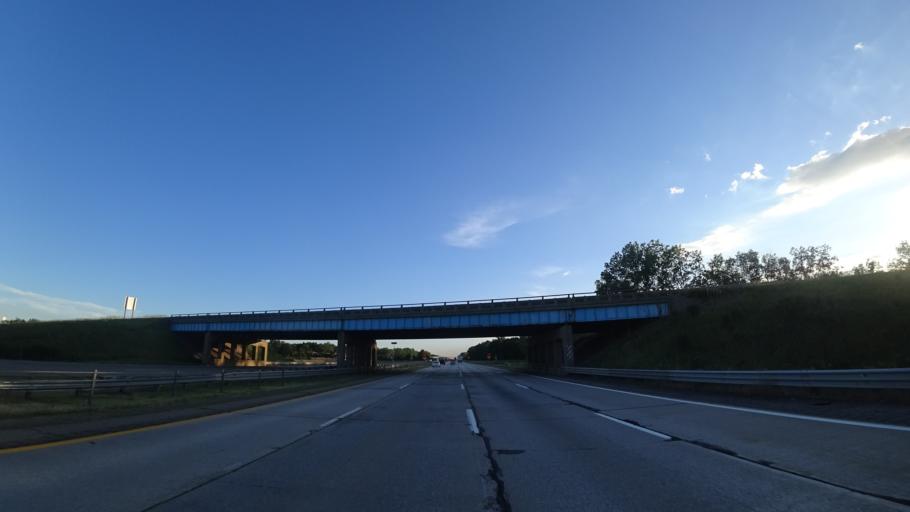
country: US
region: Michigan
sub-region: Berrien County
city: New Buffalo
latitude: 41.7752
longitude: -86.7303
